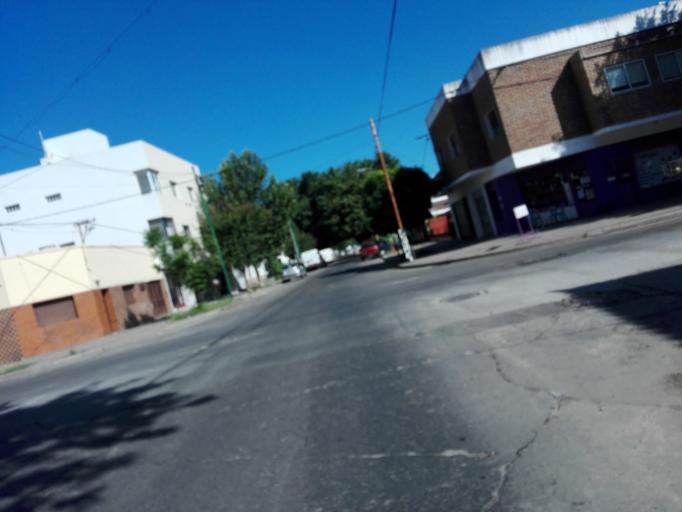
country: AR
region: Buenos Aires
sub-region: Partido de La Plata
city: La Plata
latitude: -34.9404
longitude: -57.9612
